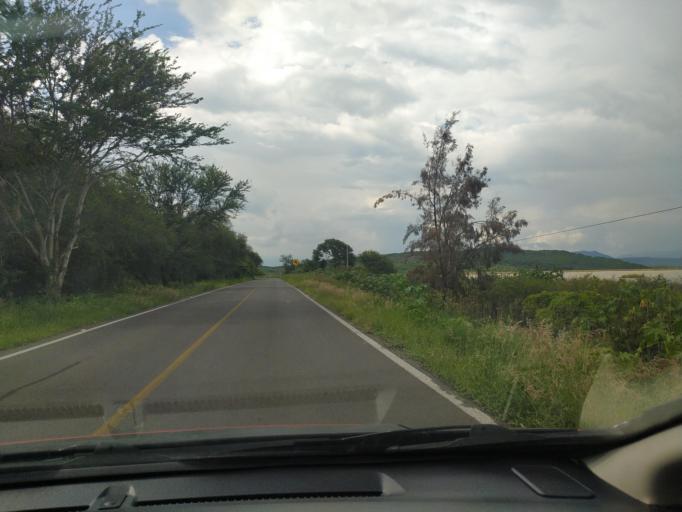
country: MX
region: Jalisco
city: Villa Corona
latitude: 20.3580
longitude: -103.6666
